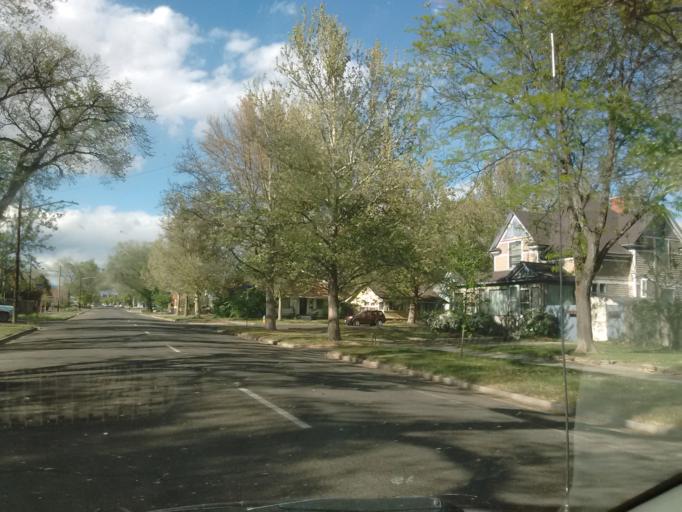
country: US
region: Colorado
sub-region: Mesa County
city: Grand Junction
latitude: 39.0740
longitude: -108.5645
